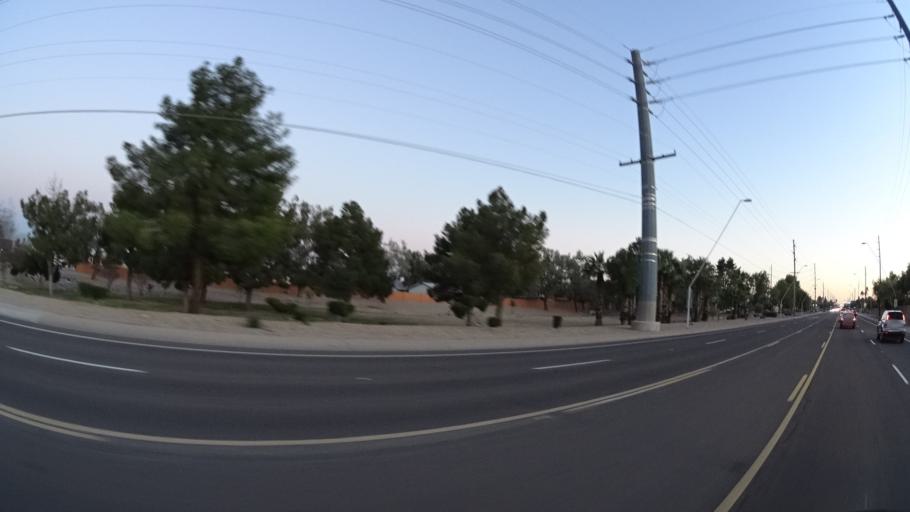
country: US
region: Arizona
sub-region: Maricopa County
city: San Carlos
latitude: 33.3296
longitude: -111.8765
